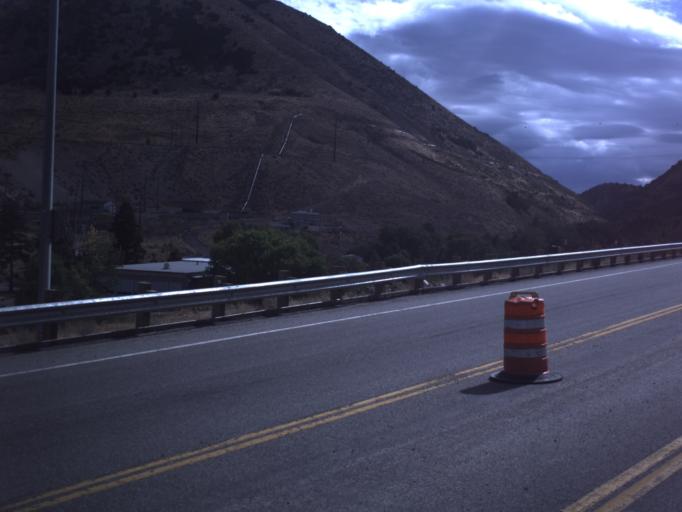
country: US
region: Utah
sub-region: Box Elder County
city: Brigham City
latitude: 41.5008
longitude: -111.9959
